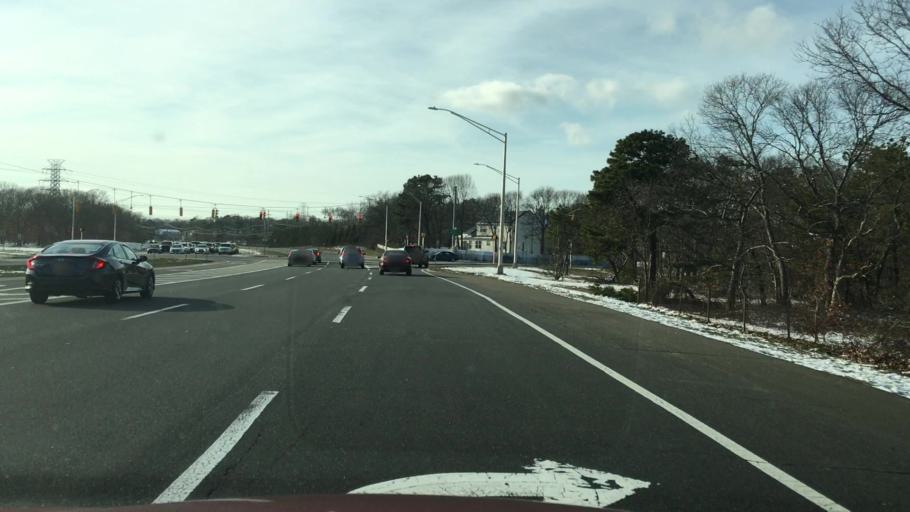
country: US
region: New York
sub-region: Suffolk County
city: Terryville
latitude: 40.8808
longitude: -73.0774
